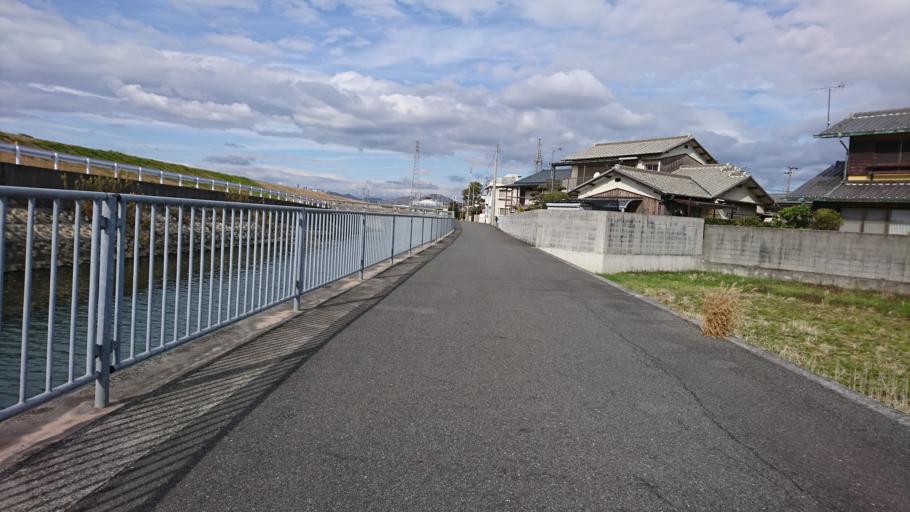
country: JP
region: Hyogo
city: Kakogawacho-honmachi
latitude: 34.7504
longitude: 134.8128
